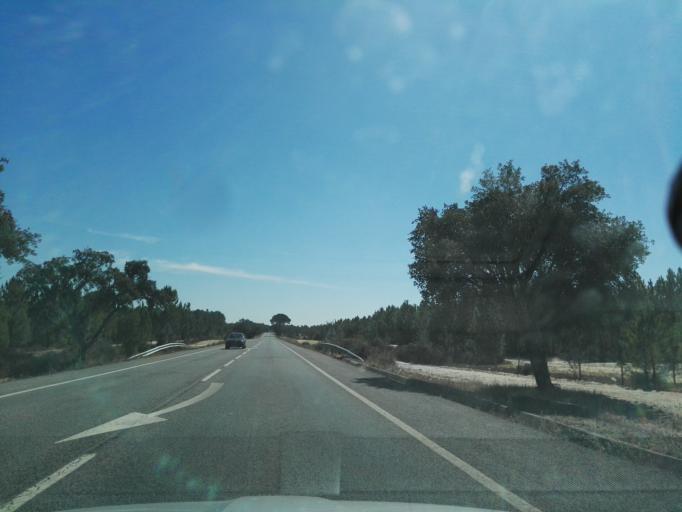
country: PT
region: Santarem
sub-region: Benavente
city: Poceirao
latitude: 38.8819
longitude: -8.8166
